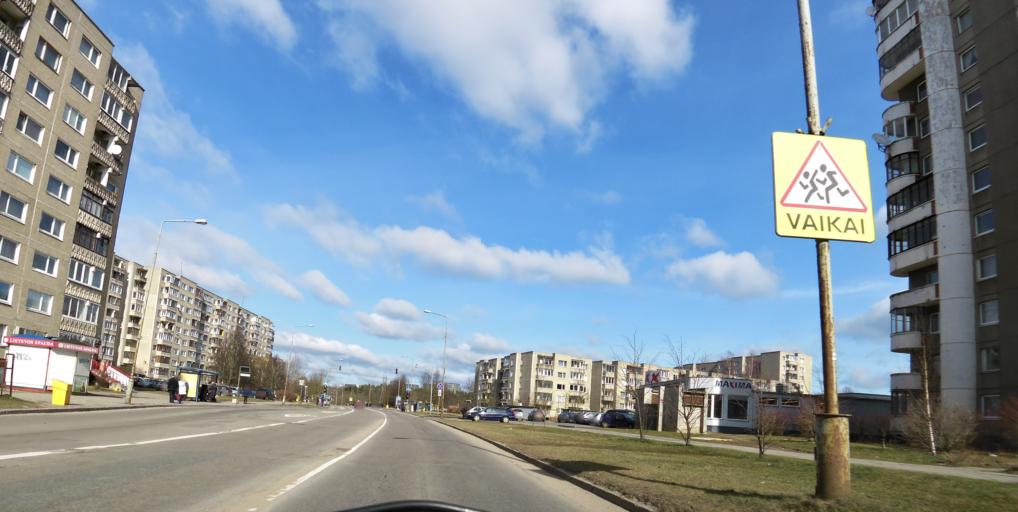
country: LT
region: Vilnius County
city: Seskine
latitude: 54.7173
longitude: 25.2579
